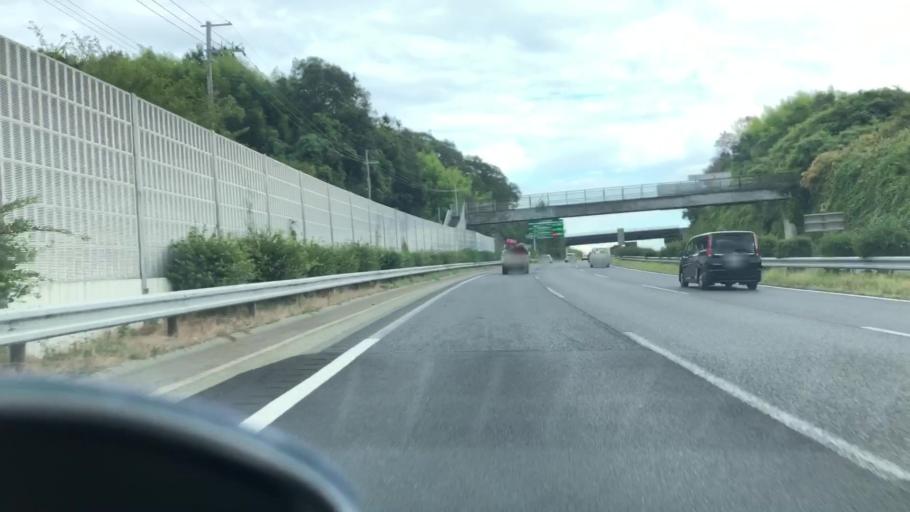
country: JP
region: Hyogo
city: Sandacho
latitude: 34.8906
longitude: 135.1594
